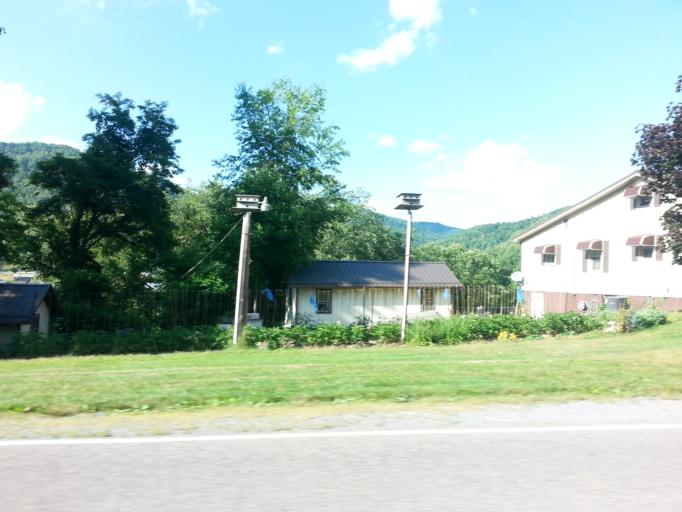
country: US
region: Virginia
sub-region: Lee County
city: Pennington Gap
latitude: 36.7658
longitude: -83.0292
